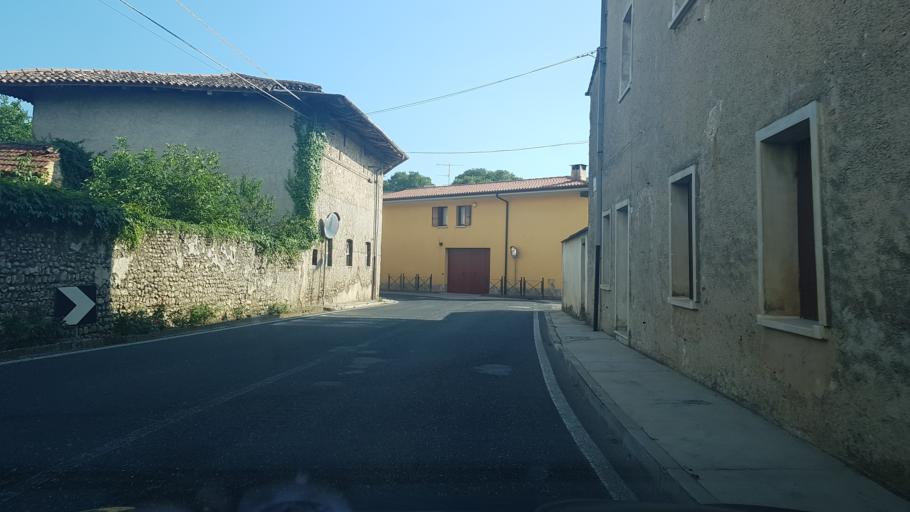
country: IT
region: Friuli Venezia Giulia
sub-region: Provincia di Udine
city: Basiliano-Vissandone
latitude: 46.0577
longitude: 13.0851
